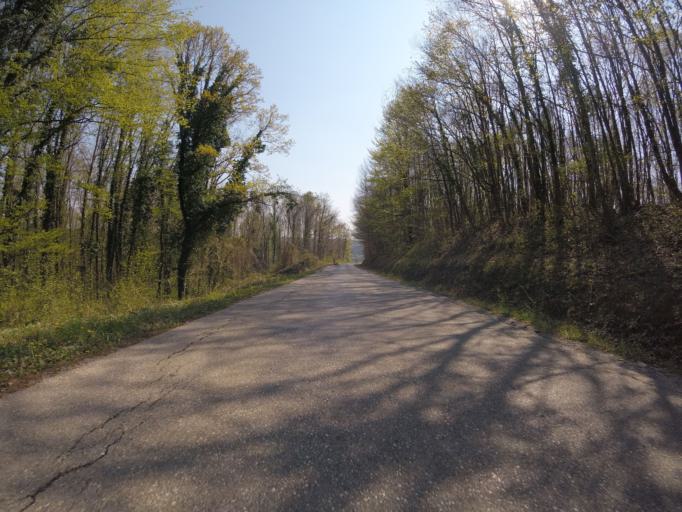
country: HR
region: Grad Zagreb
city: Strmec
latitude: 45.6257
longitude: 15.9528
